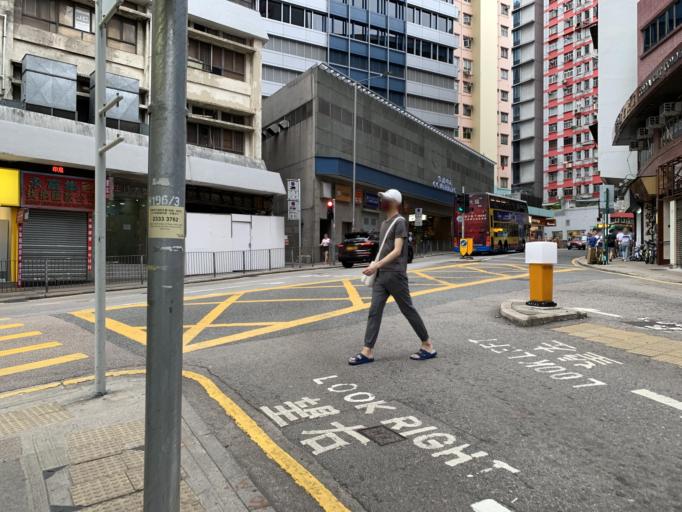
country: HK
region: Wanchai
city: Wan Chai
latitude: 22.2771
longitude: 114.1777
